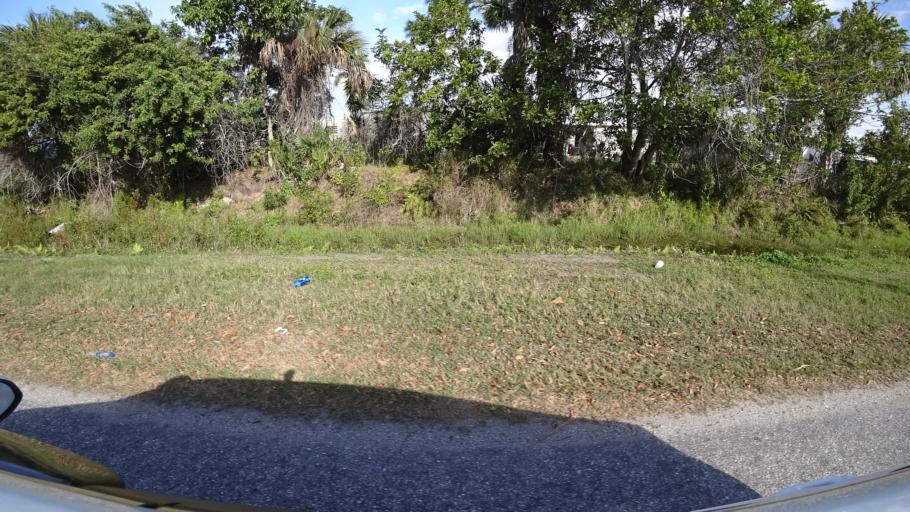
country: US
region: Florida
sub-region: Manatee County
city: Bayshore Gardens
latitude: 27.4361
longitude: -82.5711
